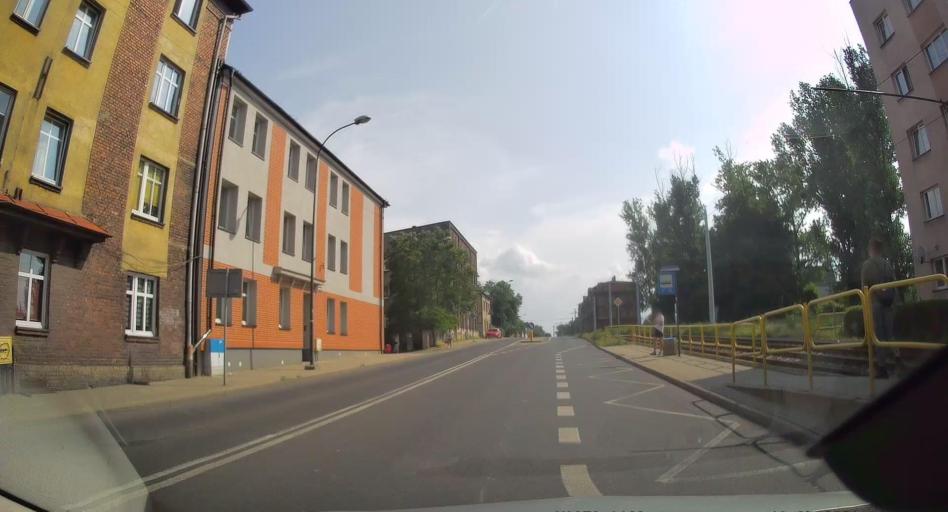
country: PL
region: Silesian Voivodeship
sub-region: Bytom
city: Bytom
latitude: 50.3234
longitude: 18.9271
